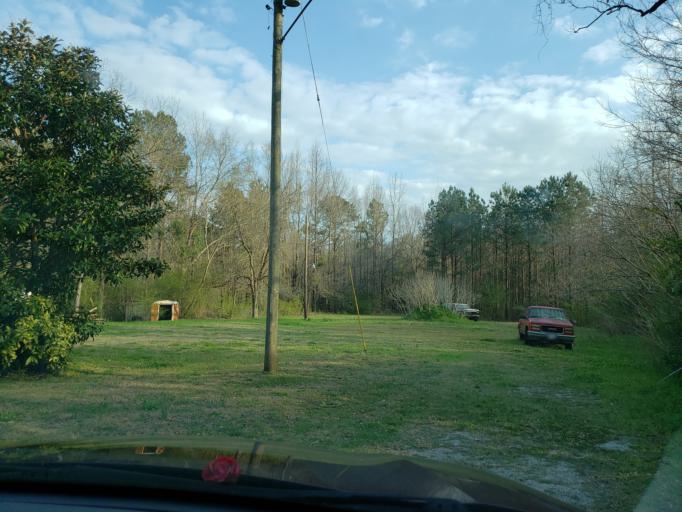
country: US
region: Alabama
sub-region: Hale County
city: Greensboro
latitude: 32.6987
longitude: -87.6054
